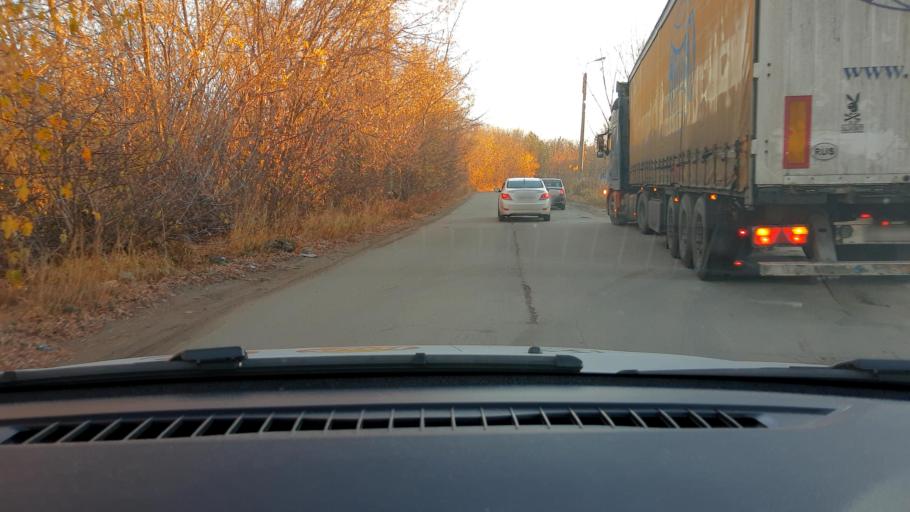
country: RU
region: Nizjnij Novgorod
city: Burevestnik
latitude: 56.2271
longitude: 43.8914
